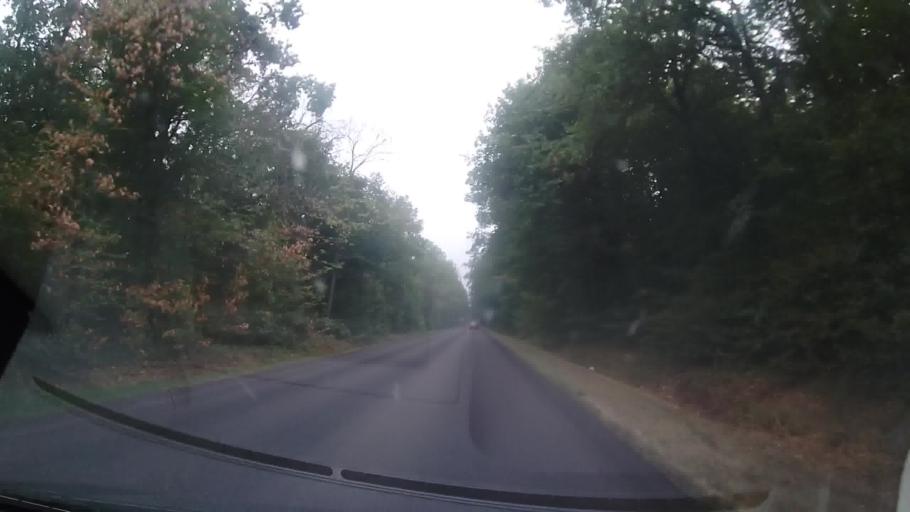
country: FR
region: Ile-de-France
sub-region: Departement de l'Essonne
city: Dourdan
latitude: 48.5447
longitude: 1.9904
